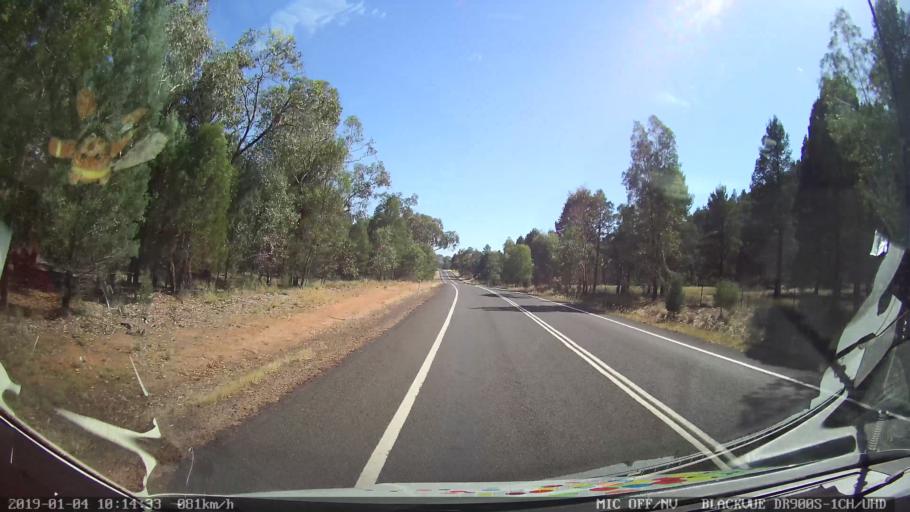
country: AU
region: New South Wales
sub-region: Cabonne
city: Canowindra
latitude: -33.3959
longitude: 148.4144
